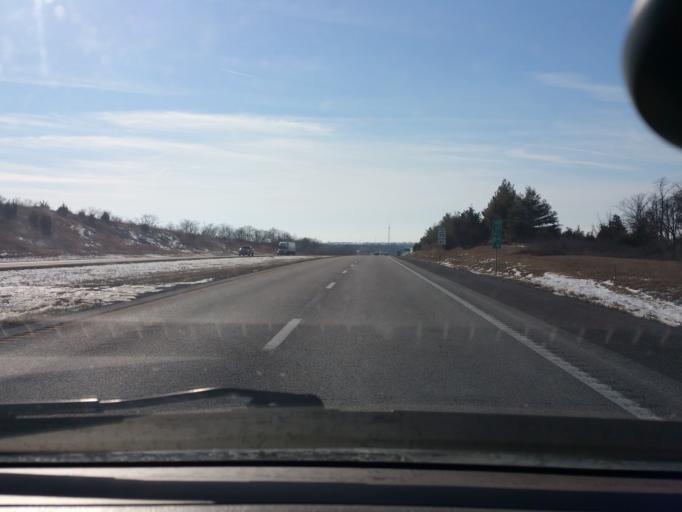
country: US
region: Missouri
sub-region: Clinton County
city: Cameron
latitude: 39.8927
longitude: -94.1553
